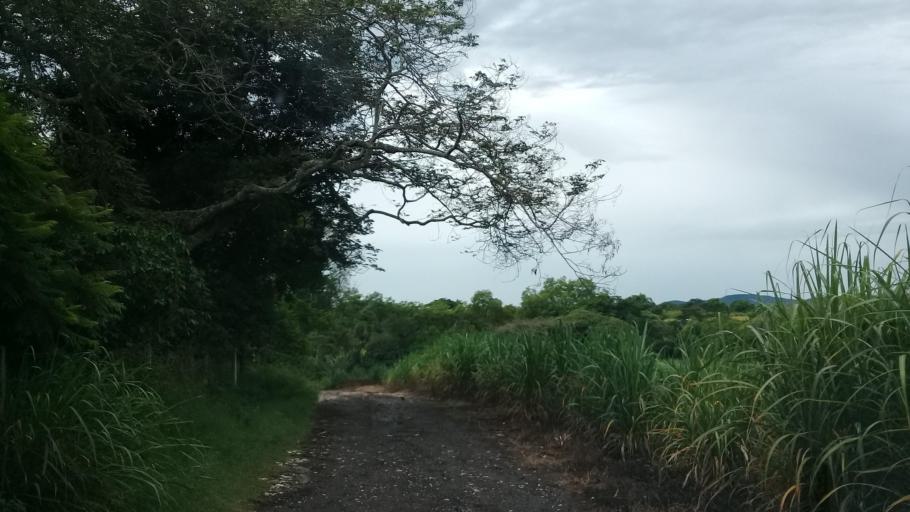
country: MX
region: Veracruz
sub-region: Emiliano Zapata
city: Dos Rios
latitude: 19.4812
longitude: -96.8098
